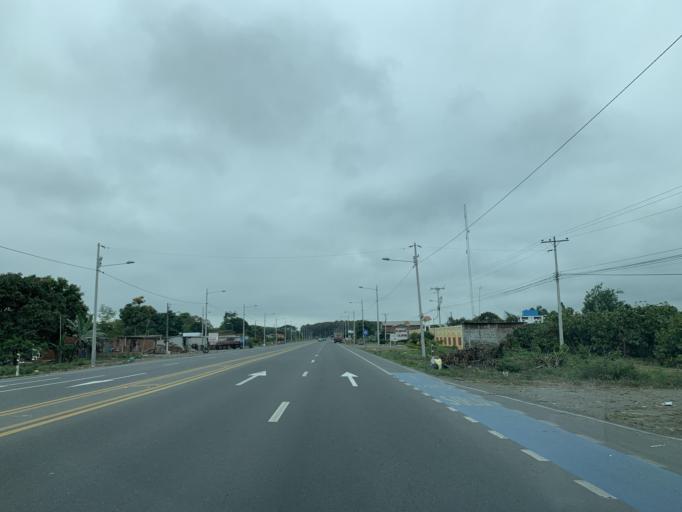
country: EC
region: Guayas
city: Coronel Marcelino Mariduena
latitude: -2.3204
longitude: -79.4634
